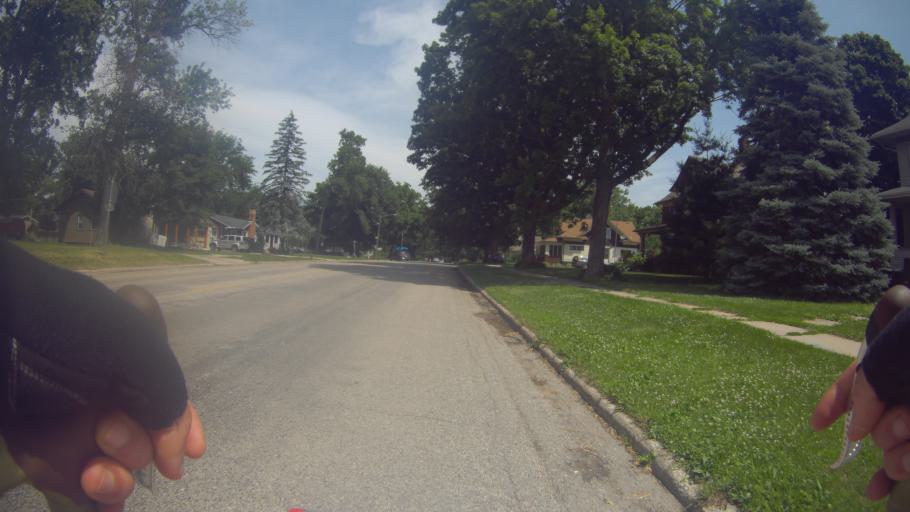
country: US
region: Wisconsin
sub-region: Jefferson County
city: Lake Mills
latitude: 43.0733
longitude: -88.9137
